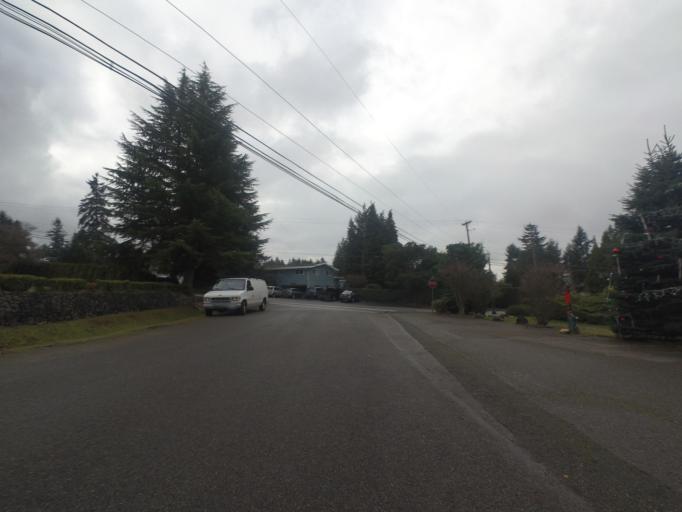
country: US
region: Washington
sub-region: Pierce County
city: University Place
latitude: 47.2184
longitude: -122.5487
